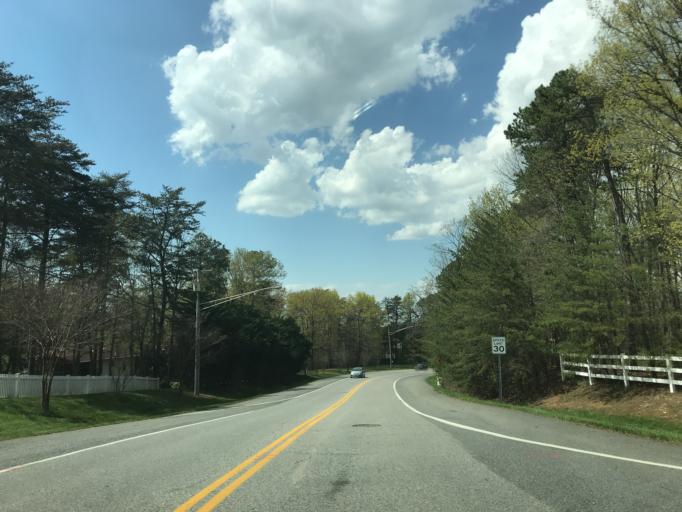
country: US
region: Maryland
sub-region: Anne Arundel County
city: Odenton
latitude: 39.0920
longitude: -76.6809
